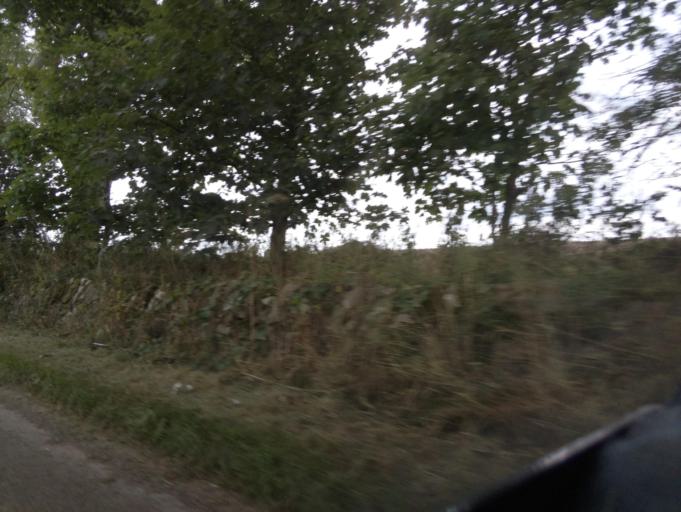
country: GB
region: Scotland
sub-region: Fife
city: Saint Andrews
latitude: 56.3142
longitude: -2.7795
